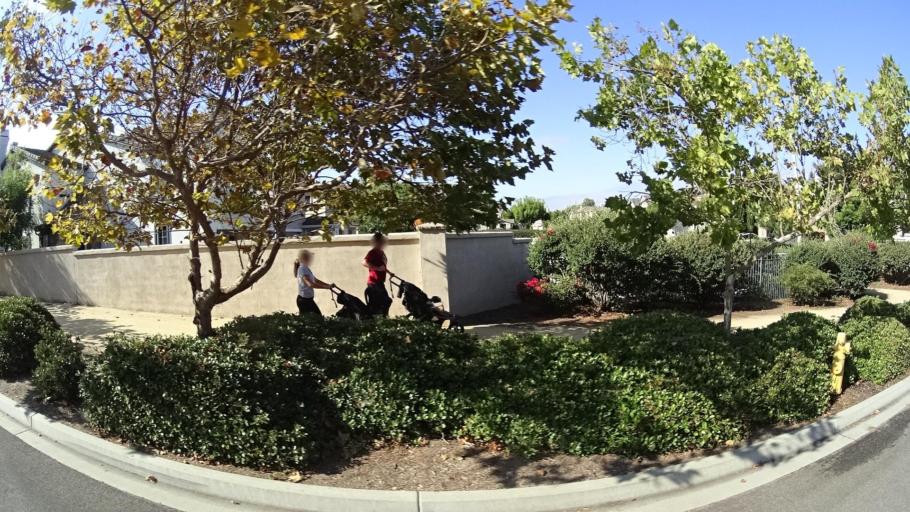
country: US
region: California
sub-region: San Diego County
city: Lake San Marcos
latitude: 33.0968
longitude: -117.1843
